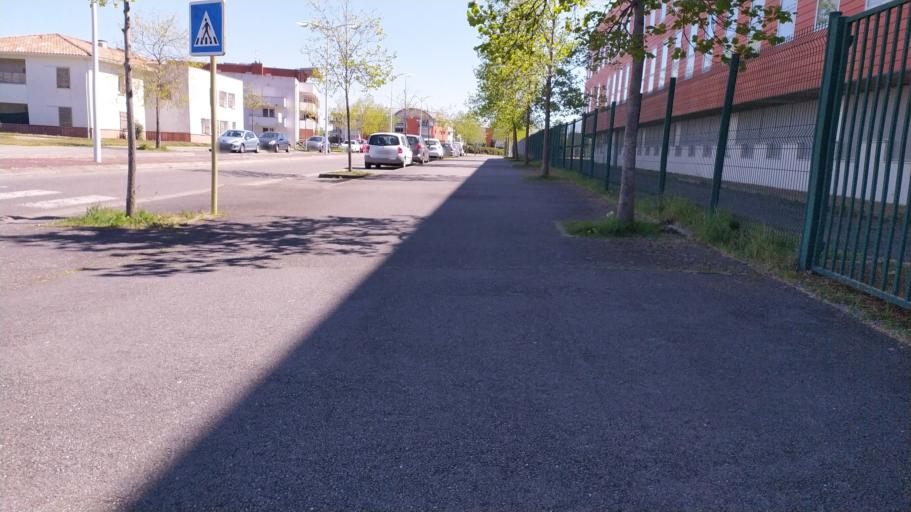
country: FR
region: Midi-Pyrenees
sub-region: Departement de la Haute-Garonne
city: Tournefeuille
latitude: 43.5778
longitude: 1.3120
